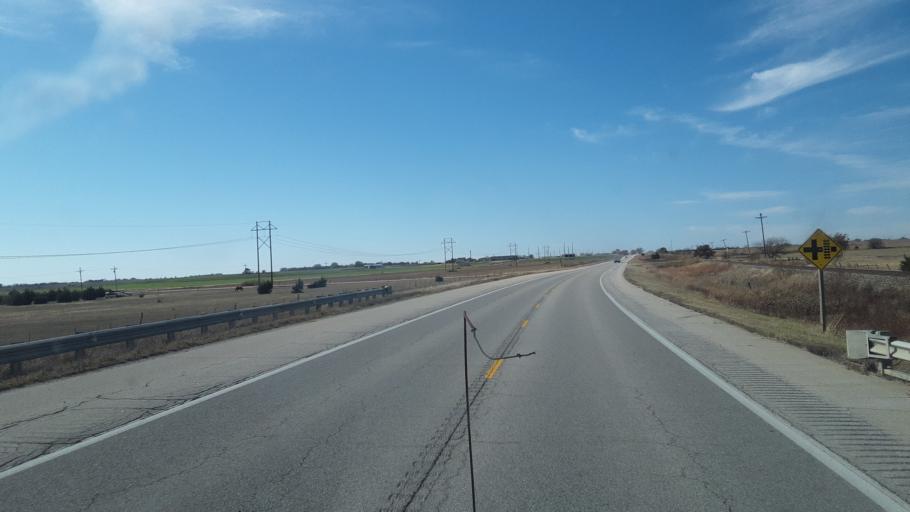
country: US
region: Kansas
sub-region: McPherson County
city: McPherson
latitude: 38.3642
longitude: -97.7563
